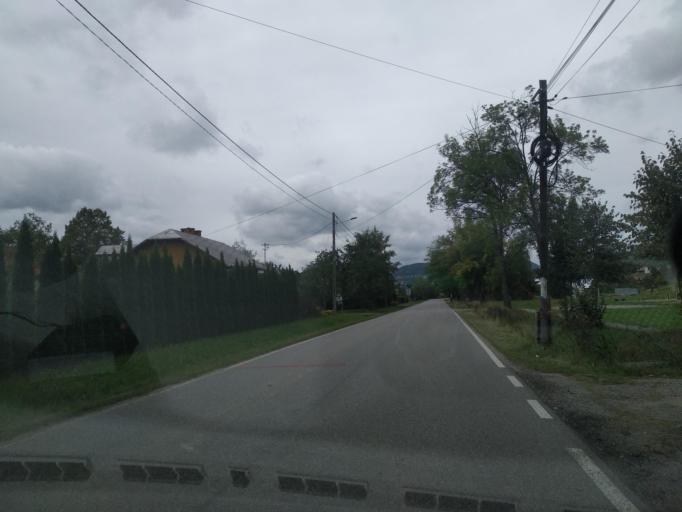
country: PL
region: Lesser Poland Voivodeship
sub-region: Powiat gorlicki
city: Ropa
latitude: 49.5724
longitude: 21.0860
